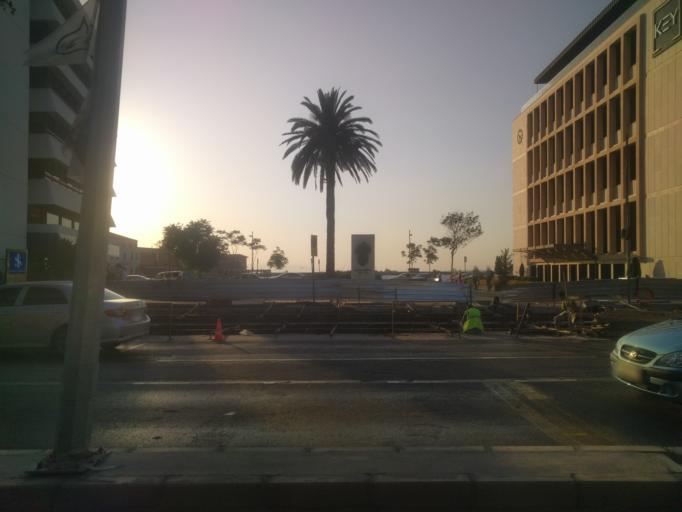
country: TR
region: Izmir
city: Izmir
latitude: 38.4231
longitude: 27.1313
